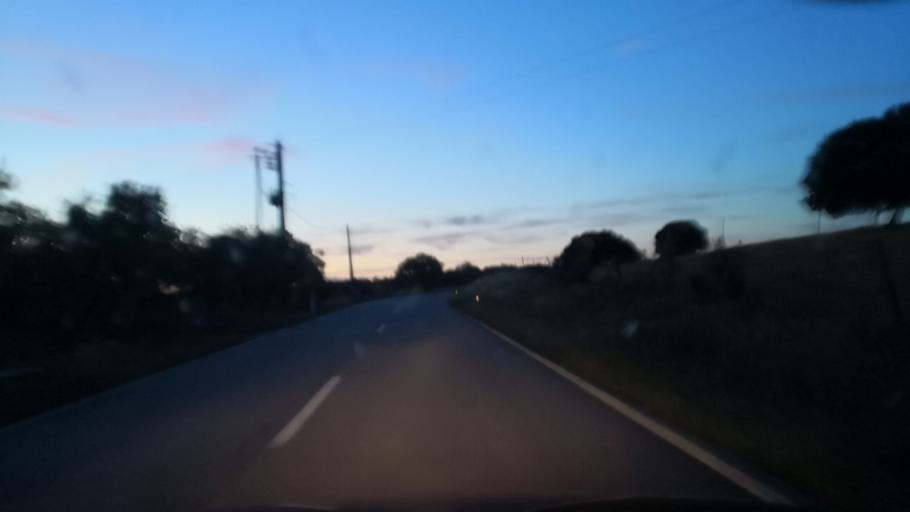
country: ES
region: Extremadura
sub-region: Provincia de Caceres
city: Piedras Albas
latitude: 39.8452
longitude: -6.9800
